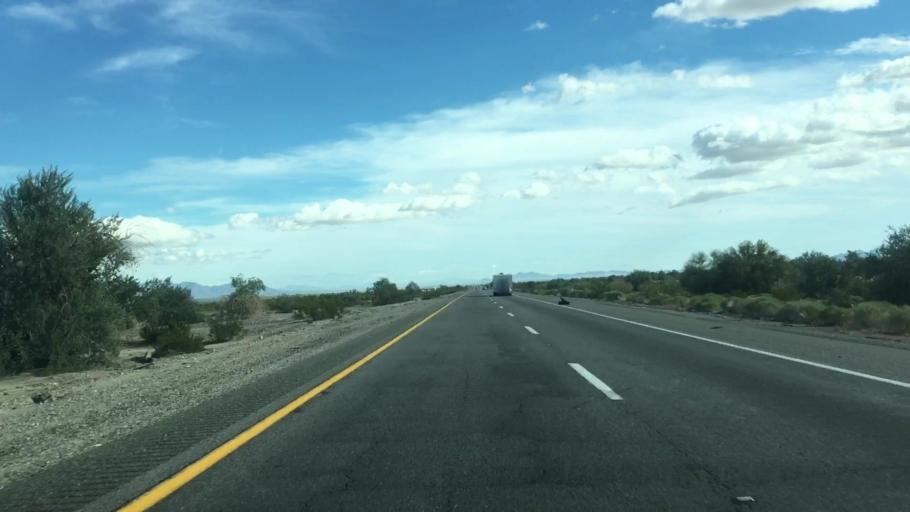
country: US
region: California
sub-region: Riverside County
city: Mesa Verde
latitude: 33.6744
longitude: -115.2169
